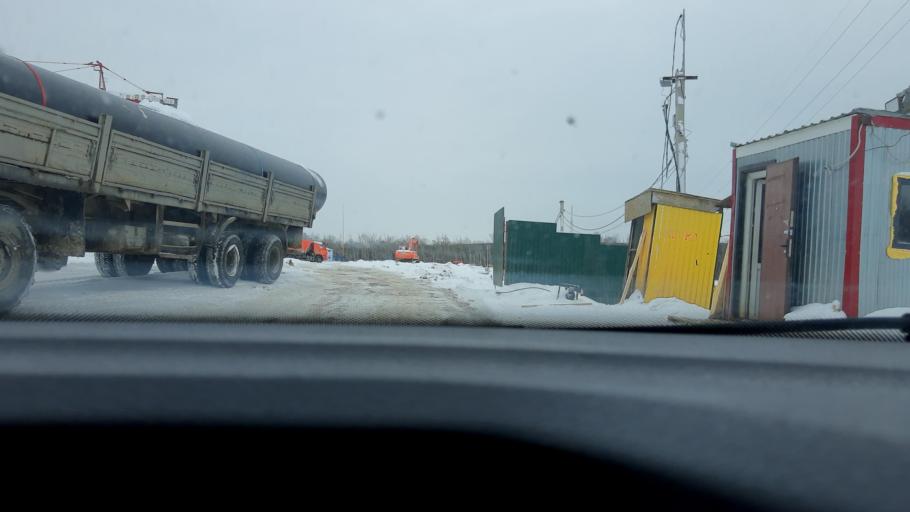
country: RU
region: Bashkortostan
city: Ufa
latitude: 54.7785
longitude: 55.9602
